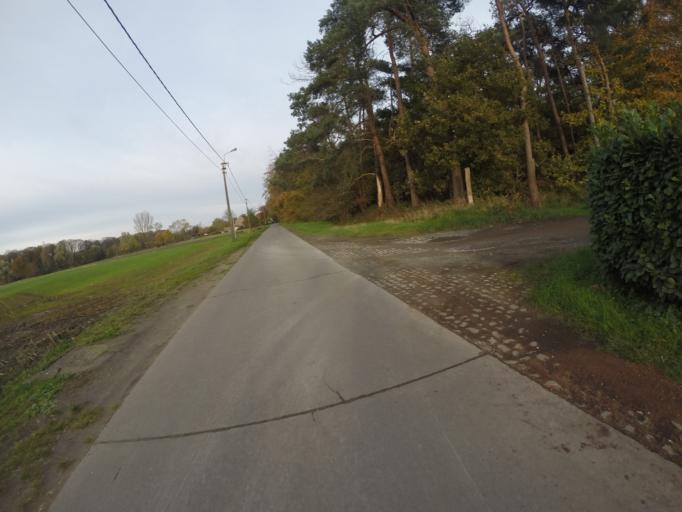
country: BE
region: Flanders
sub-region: Provincie Oost-Vlaanderen
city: Aalter
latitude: 51.0714
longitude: 3.4957
